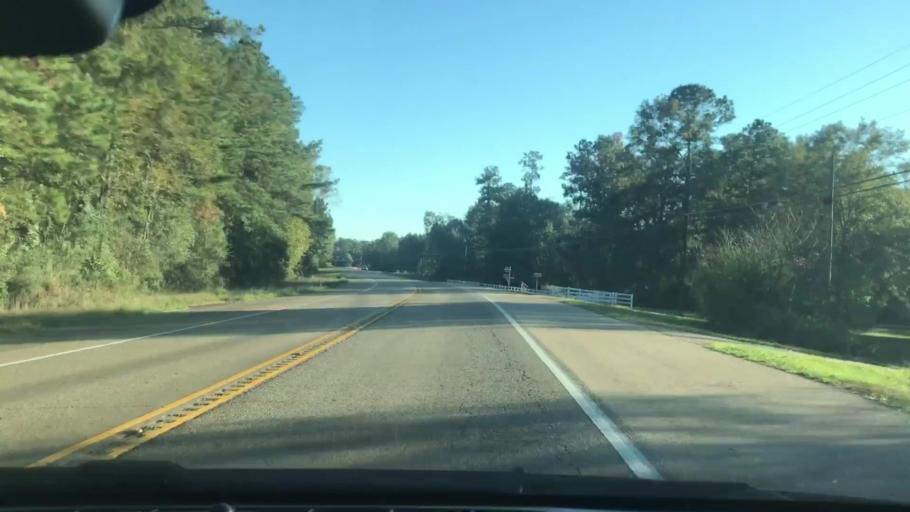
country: US
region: Louisiana
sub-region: Washington Parish
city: Bogalusa
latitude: 30.6002
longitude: -89.8726
